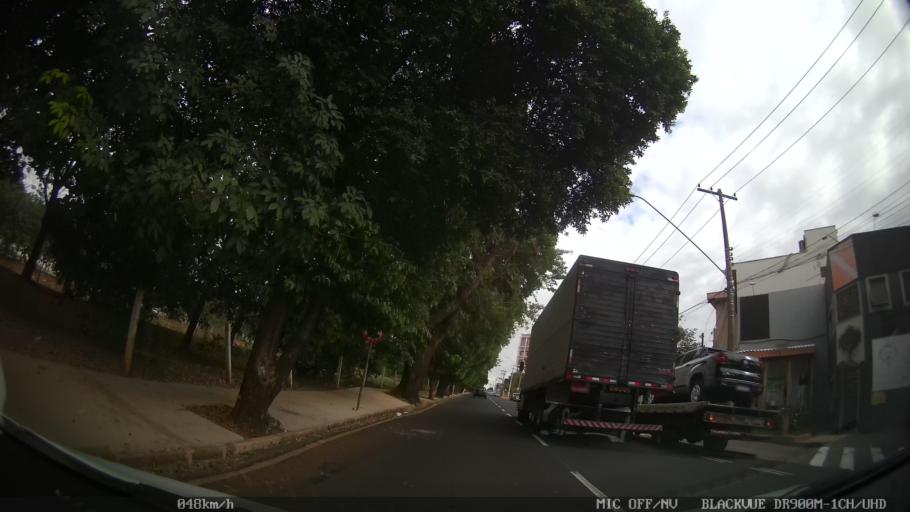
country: BR
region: Sao Paulo
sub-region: Sao Jose Do Rio Preto
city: Sao Jose do Rio Preto
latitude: -20.8230
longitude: -49.3886
